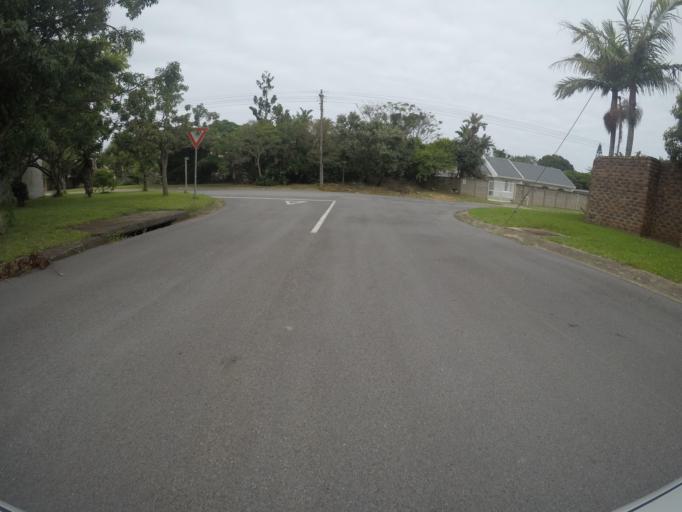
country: ZA
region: Eastern Cape
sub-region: Buffalo City Metropolitan Municipality
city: East London
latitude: -32.9776
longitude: 27.9489
